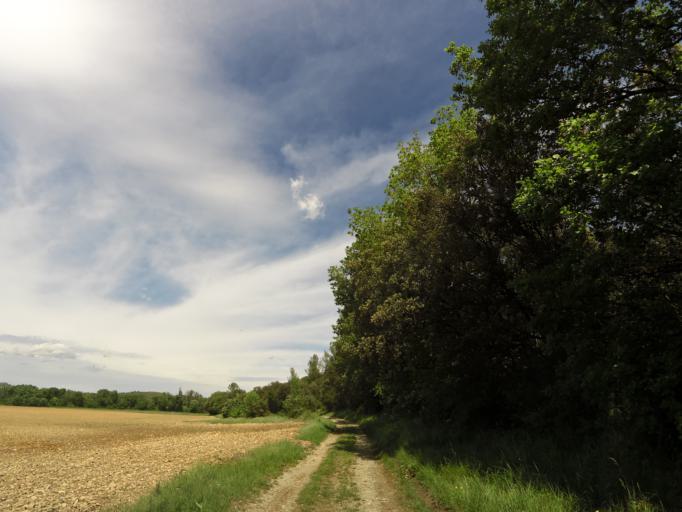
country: FR
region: Languedoc-Roussillon
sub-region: Departement du Gard
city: Quissac
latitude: 43.8791
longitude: 4.0287
